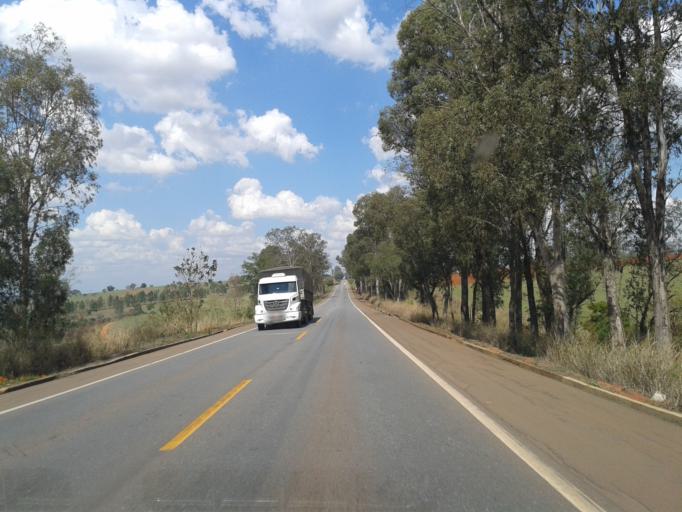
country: BR
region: Minas Gerais
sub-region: Luz
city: Luz
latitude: -19.7777
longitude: -45.7444
